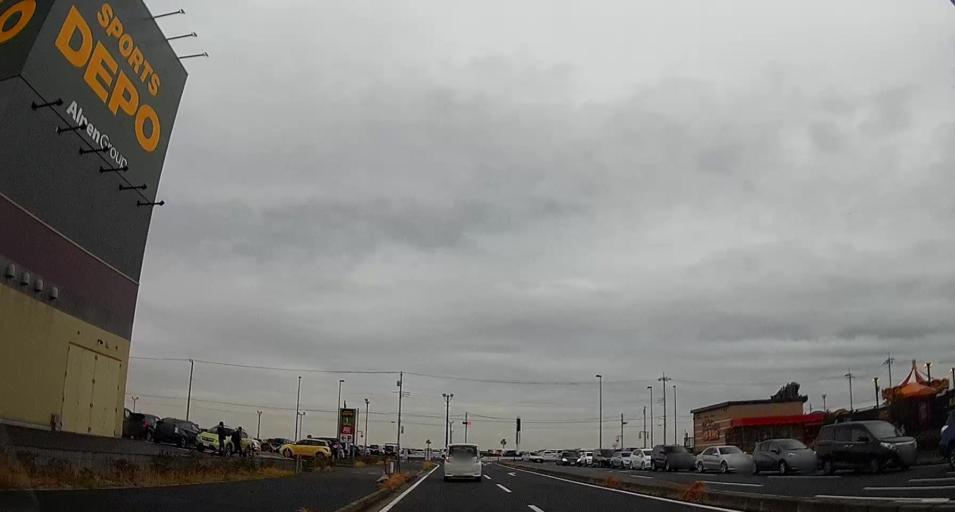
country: JP
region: Chiba
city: Kisarazu
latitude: 35.4386
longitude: 139.9321
